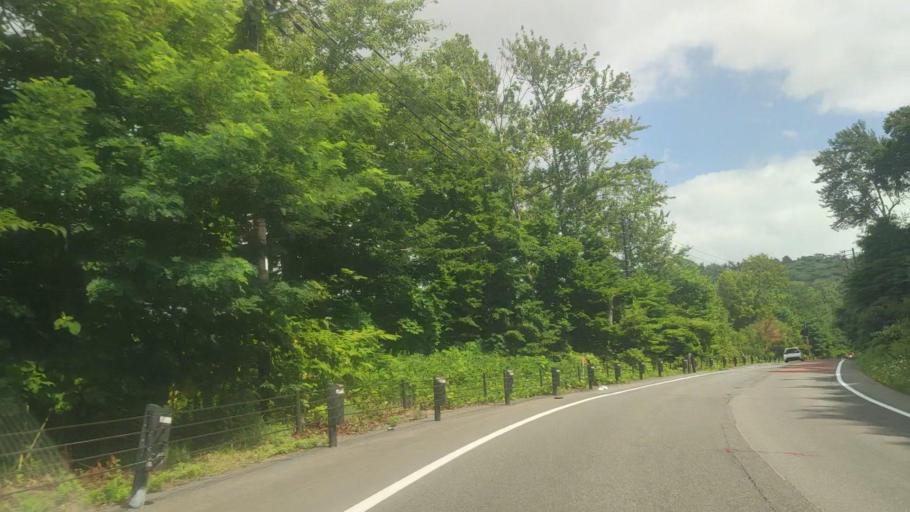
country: JP
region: Hokkaido
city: Date
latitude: 42.5650
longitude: 140.8811
